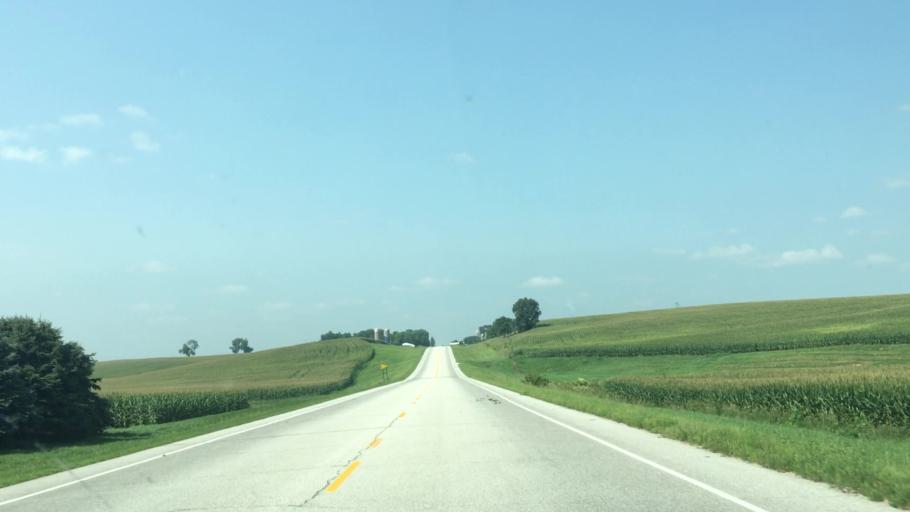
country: US
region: Minnesota
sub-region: Fillmore County
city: Harmony
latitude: 43.6052
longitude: -91.9297
